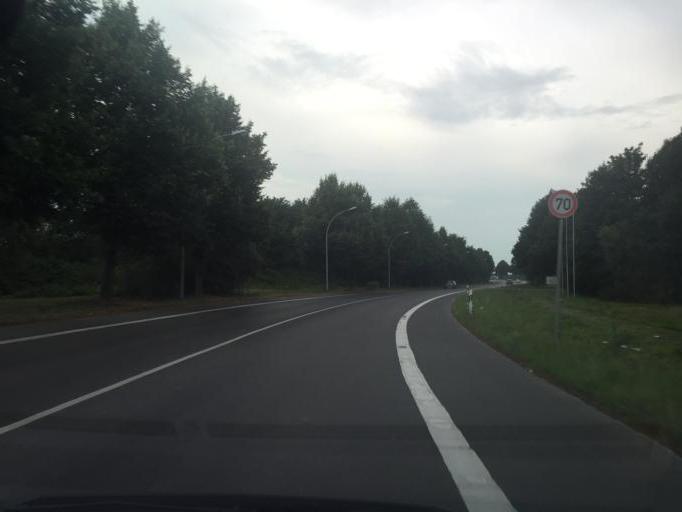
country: DE
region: North Rhine-Westphalia
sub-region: Regierungsbezirk Dusseldorf
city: Viersen
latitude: 51.1945
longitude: 6.3757
